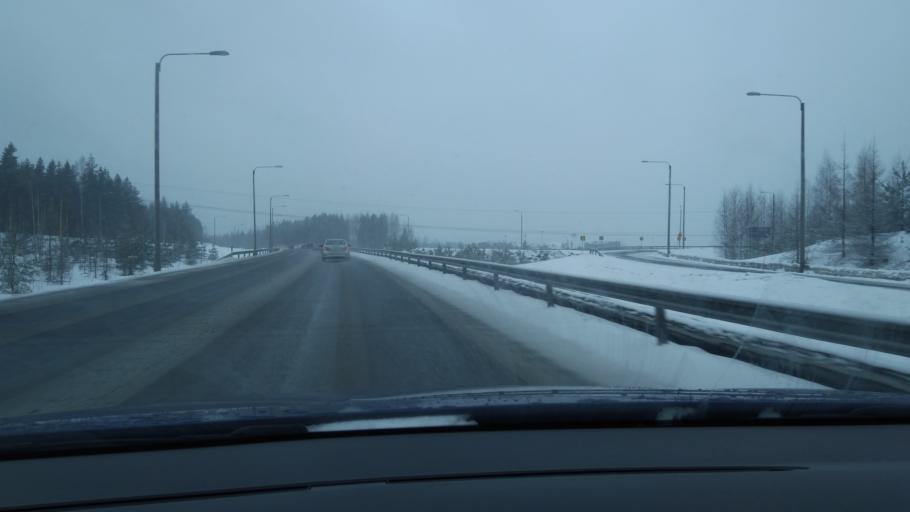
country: FI
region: Pirkanmaa
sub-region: Tampere
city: Kangasala
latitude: 61.5378
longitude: 23.9798
